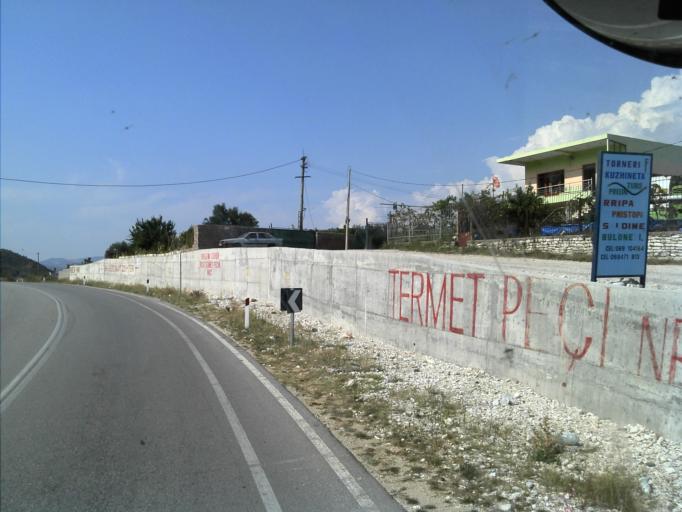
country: AL
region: Gjirokaster
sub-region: Rrethi i Tepelenes
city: Tepelene
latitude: 40.3101
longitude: 20.0163
